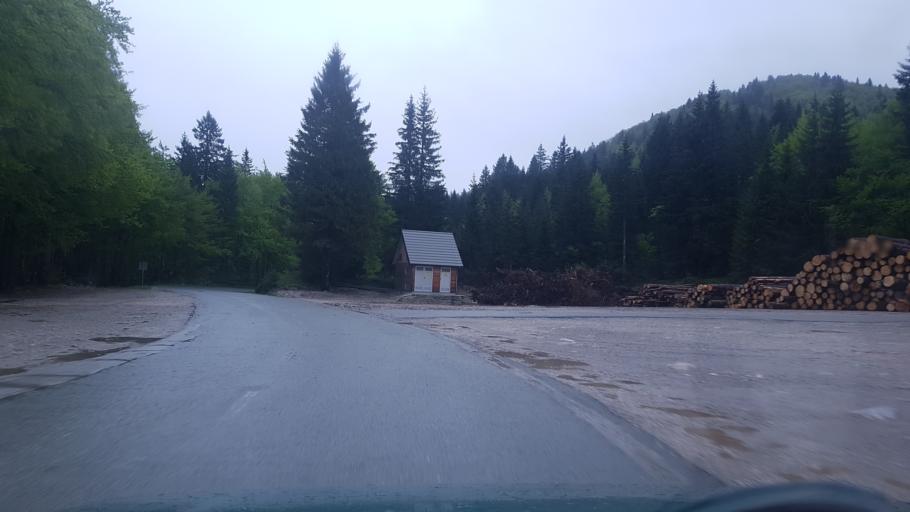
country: SI
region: Bohinj
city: Bohinjska Bistrica
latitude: 46.2409
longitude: 14.0105
